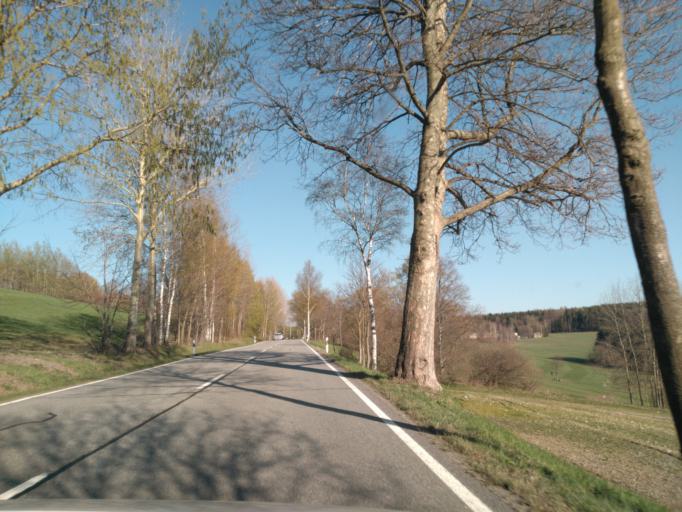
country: DE
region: Saxony
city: Schlettau
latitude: 50.5565
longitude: 12.9700
